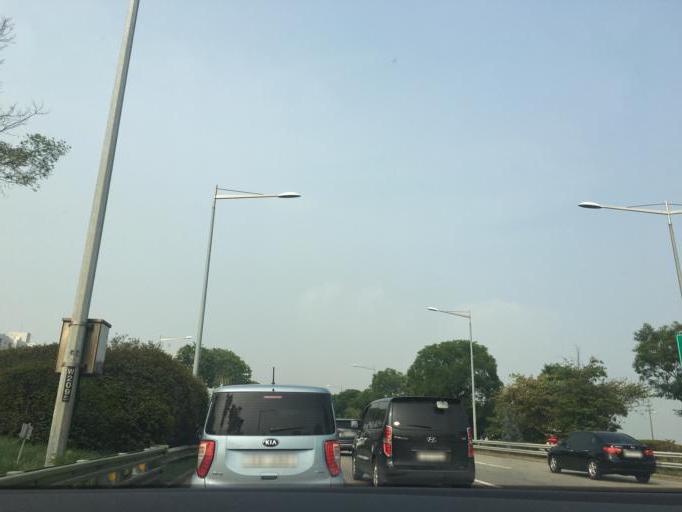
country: KR
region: Gyeonggi-do
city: Guri-si
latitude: 37.5230
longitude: 127.1008
